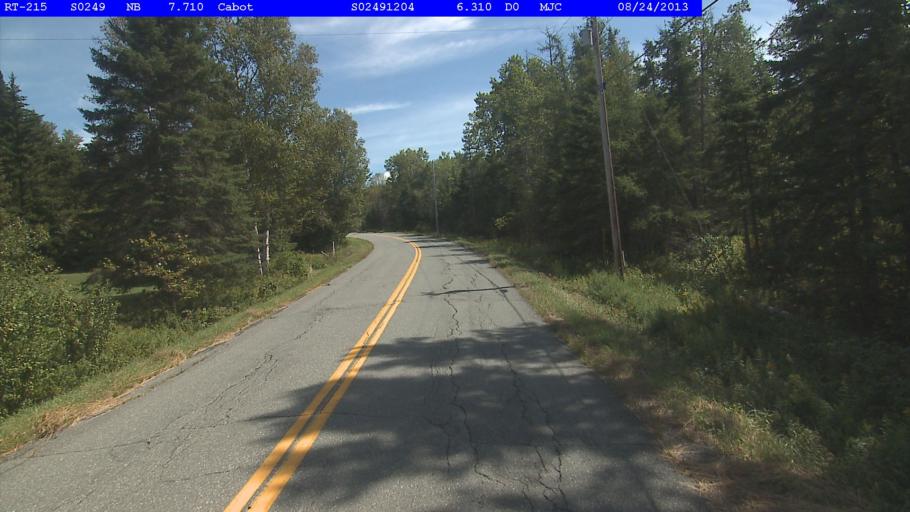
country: US
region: Vermont
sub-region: Caledonia County
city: Hardwick
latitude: 44.4389
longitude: -72.2767
